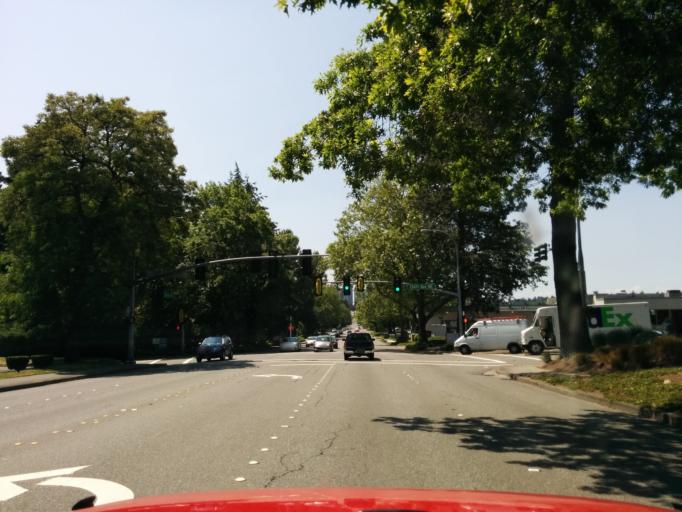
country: US
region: Washington
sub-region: King County
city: Bellevue
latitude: 47.6229
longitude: -122.1610
